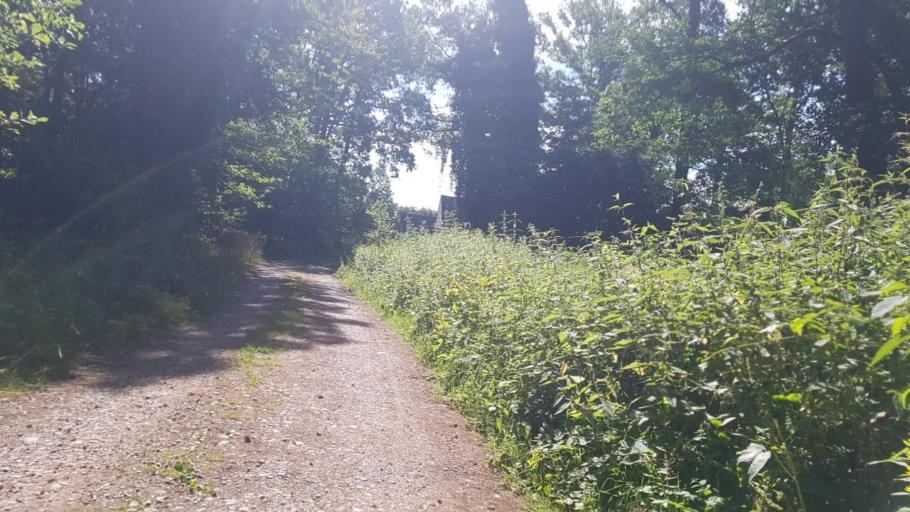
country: DE
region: North Rhine-Westphalia
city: Heimbach
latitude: 50.6175
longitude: 6.5322
